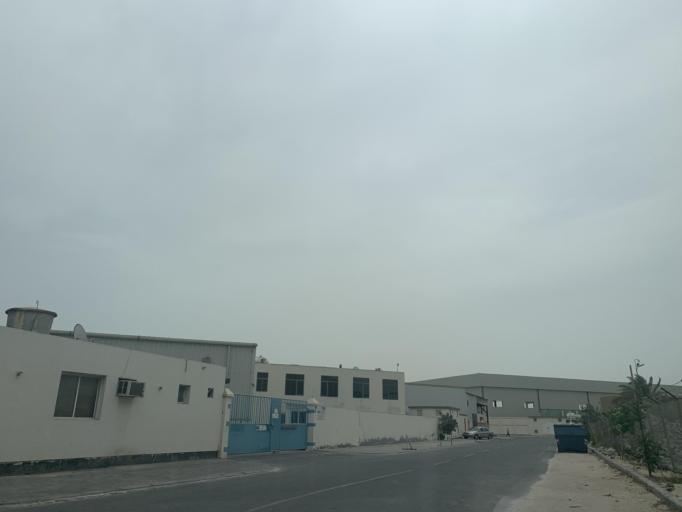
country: BH
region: Muharraq
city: Al Hadd
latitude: 26.2165
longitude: 50.6554
